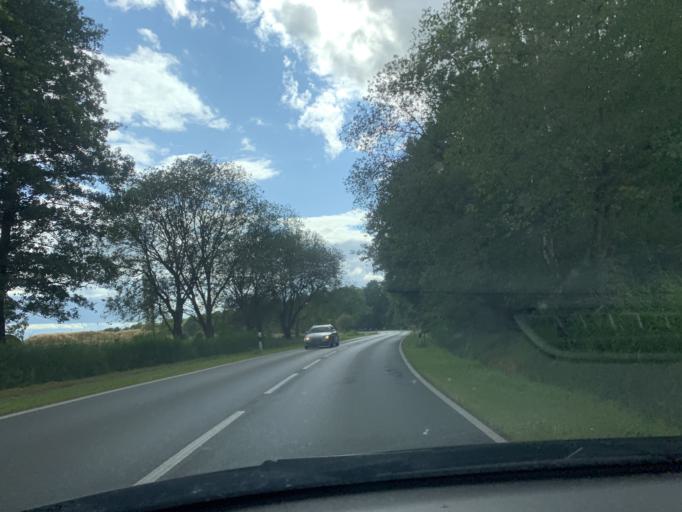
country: DE
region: Lower Saxony
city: Bad Zwischenahn
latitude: 53.2061
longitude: 8.0039
